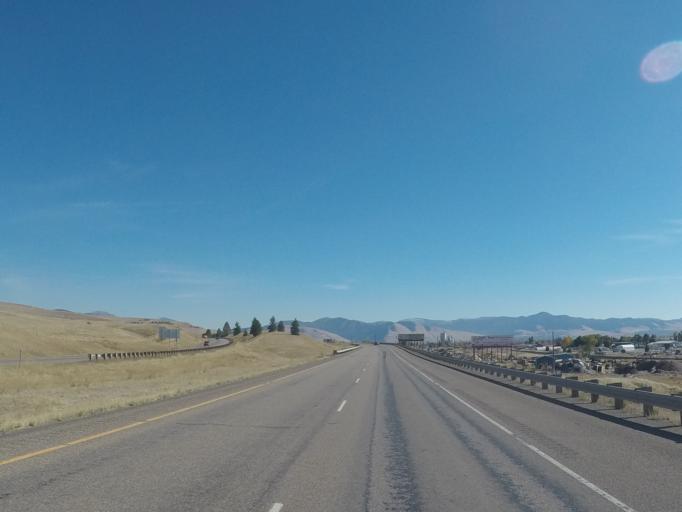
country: US
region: Montana
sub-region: Missoula County
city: Orchard Homes
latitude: 46.9413
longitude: -114.1139
